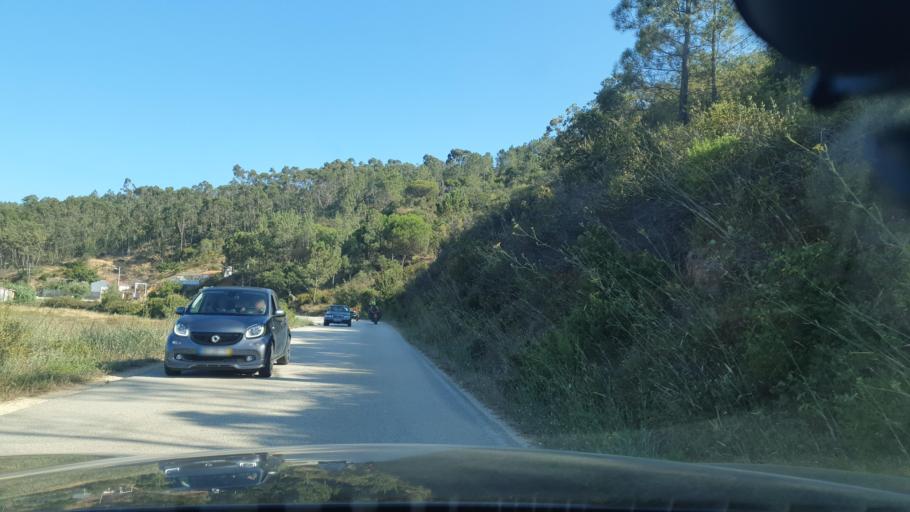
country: PT
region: Beja
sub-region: Odemira
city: Sao Teotonio
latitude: 37.4341
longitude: -8.7851
